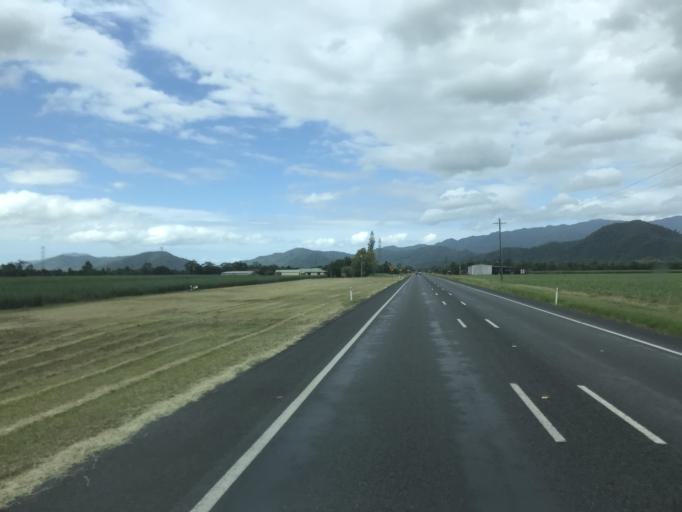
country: AU
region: Queensland
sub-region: Cassowary Coast
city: Innisfail
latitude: -17.7845
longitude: 146.0245
